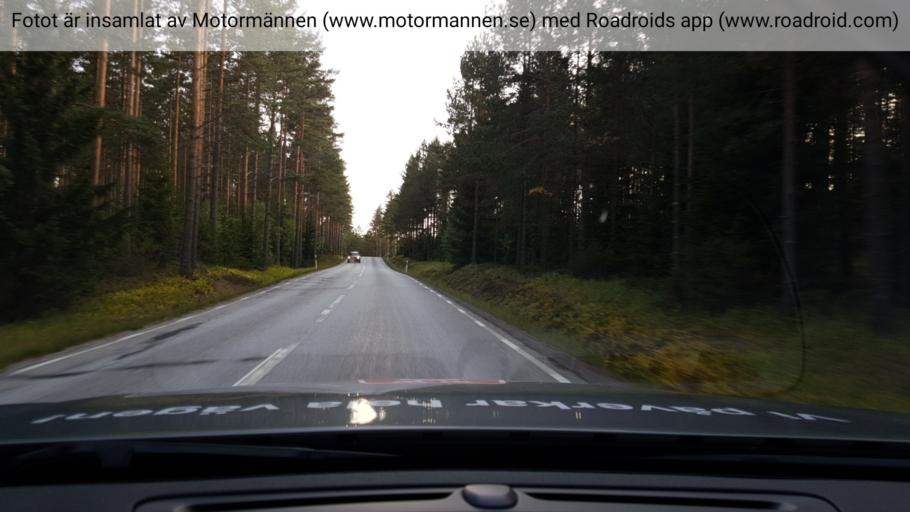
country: SE
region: OErebro
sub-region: Ljusnarsbergs Kommun
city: Kopparberg
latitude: 59.7913
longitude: 14.8122
